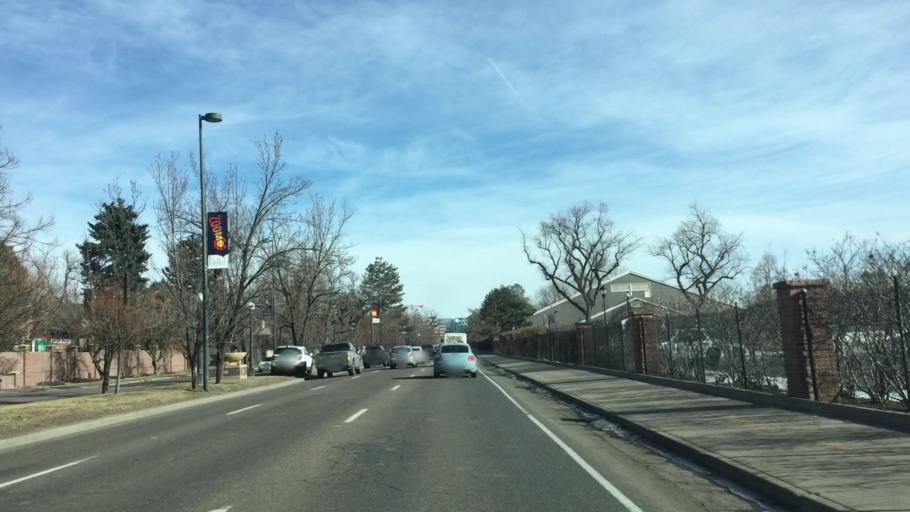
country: US
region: Colorado
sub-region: Denver County
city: Denver
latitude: 39.7181
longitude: -104.9658
